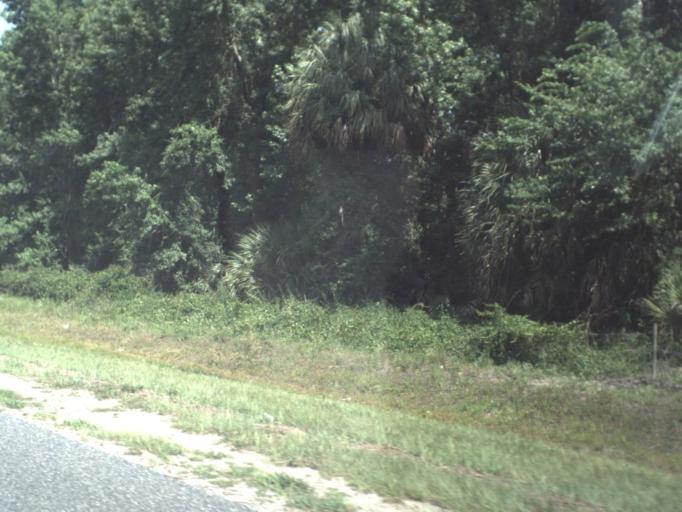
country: US
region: Florida
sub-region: Putnam County
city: Palatka
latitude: 29.6317
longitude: -81.7348
